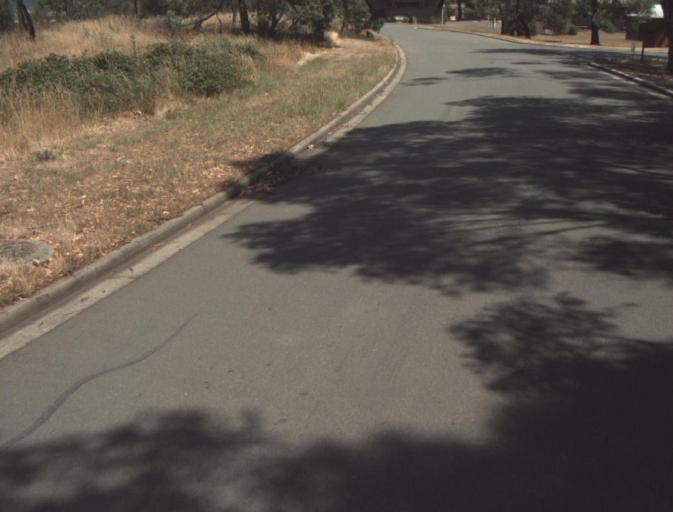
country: AU
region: Tasmania
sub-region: Launceston
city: Mayfield
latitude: -41.3747
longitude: 147.1310
